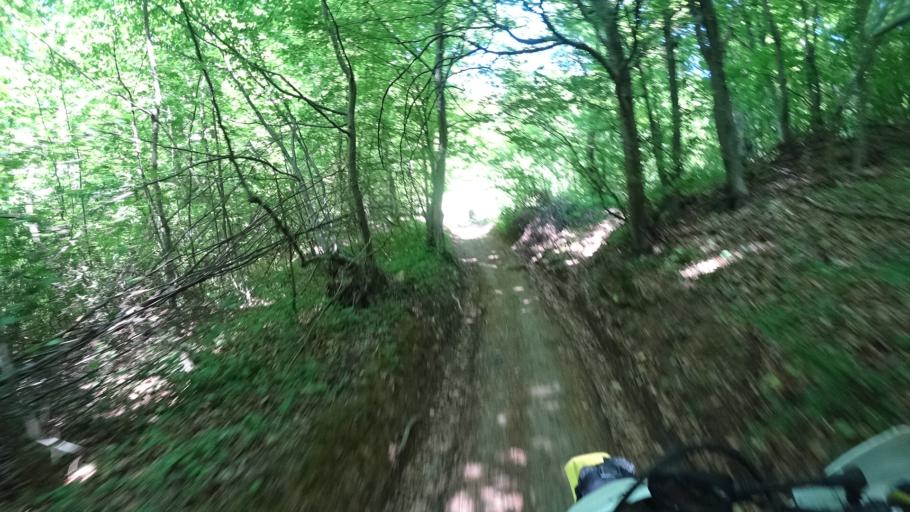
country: HR
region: Zagrebacka
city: Jablanovec
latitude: 45.8541
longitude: 15.8577
